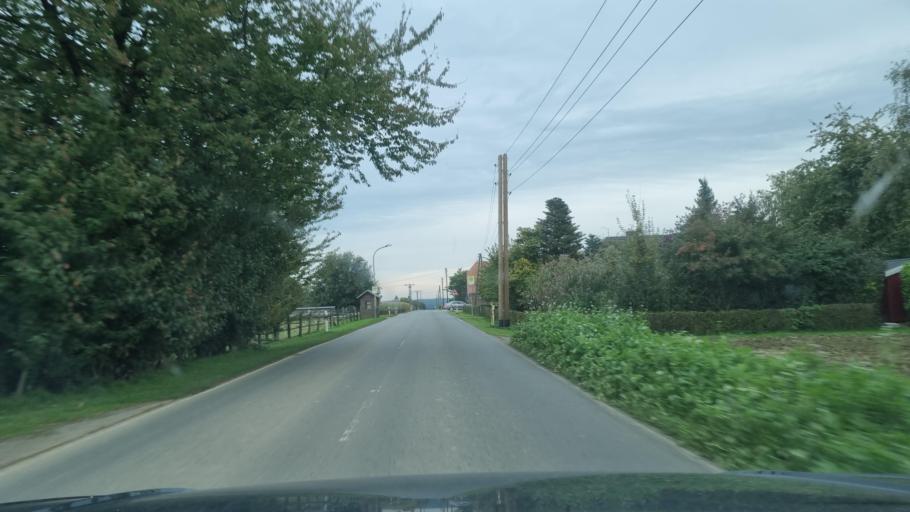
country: DE
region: North Rhine-Westphalia
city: Kalkar
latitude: 51.7074
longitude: 6.3015
